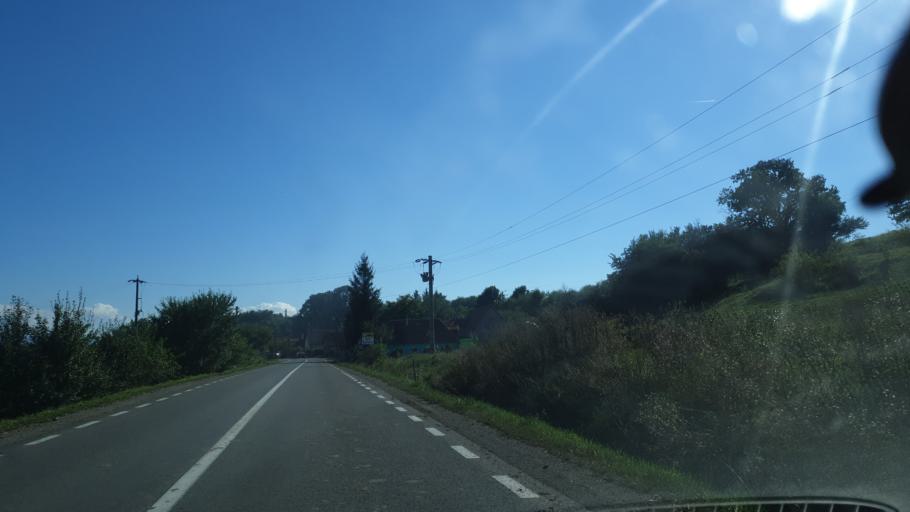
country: RO
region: Covasna
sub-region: Comuna Ilieni
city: Ilieni
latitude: 45.8045
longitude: 25.7698
